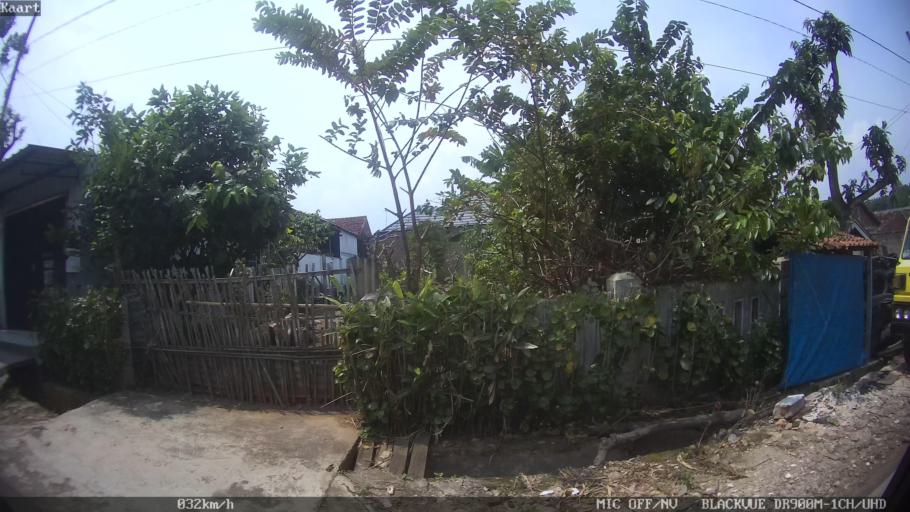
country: ID
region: Lampung
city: Bandarlampung
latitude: -5.4542
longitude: 105.2457
